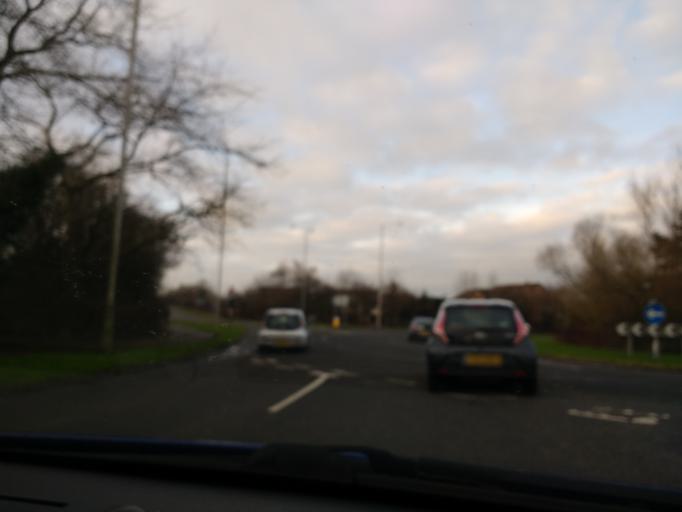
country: GB
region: England
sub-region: Lancashire
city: Lancaster
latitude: 54.0594
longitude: -2.8248
